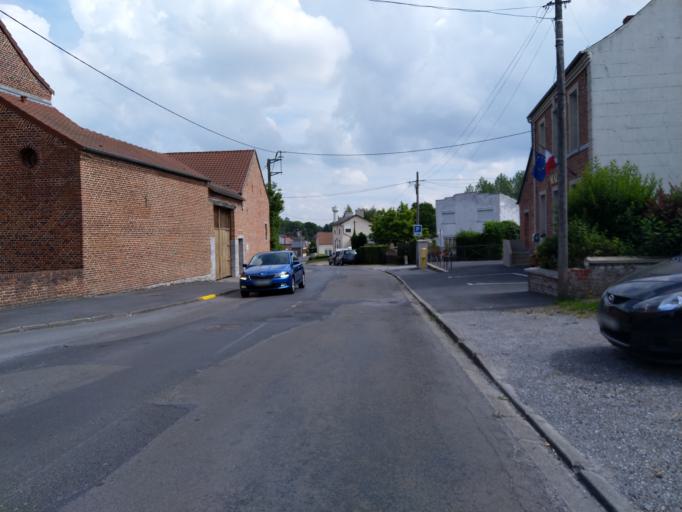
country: FR
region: Nord-Pas-de-Calais
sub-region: Departement du Nord
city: Rousies
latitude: 50.3200
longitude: 4.0043
